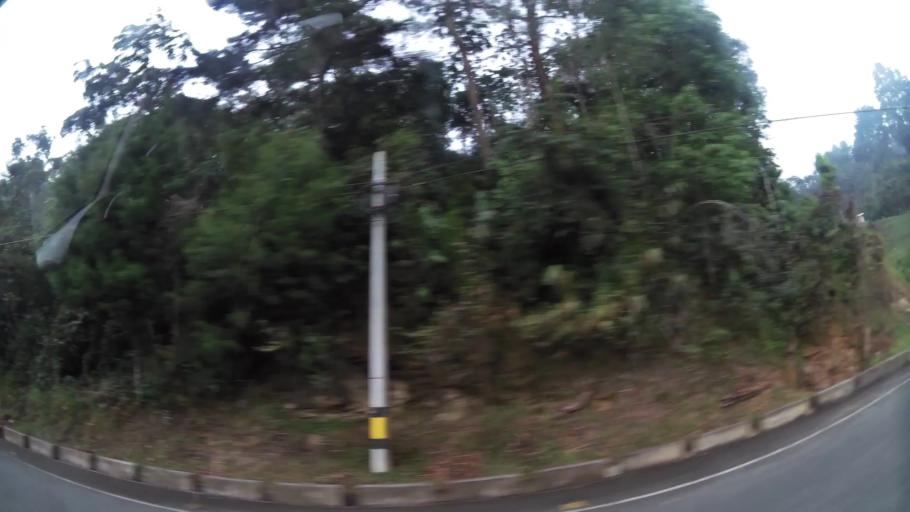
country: CO
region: Antioquia
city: Medellin
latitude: 6.2023
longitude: -75.5438
